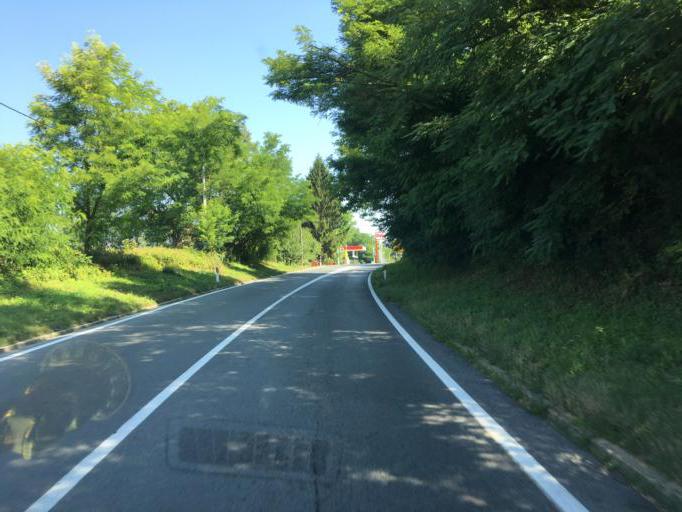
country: HR
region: Karlovacka
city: Vojnic
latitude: 45.3771
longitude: 15.6112
